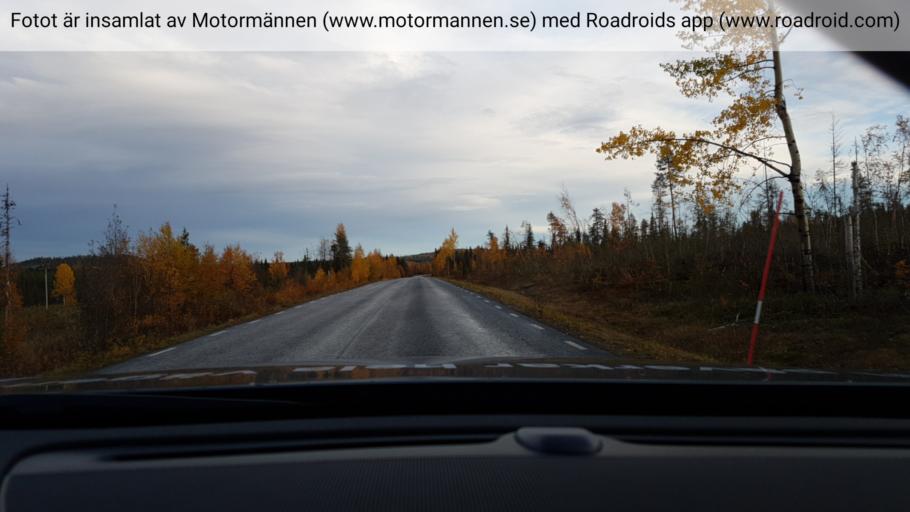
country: SE
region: Norrbotten
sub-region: Overkalix Kommun
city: OEverkalix
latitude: 66.9167
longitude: 22.7599
